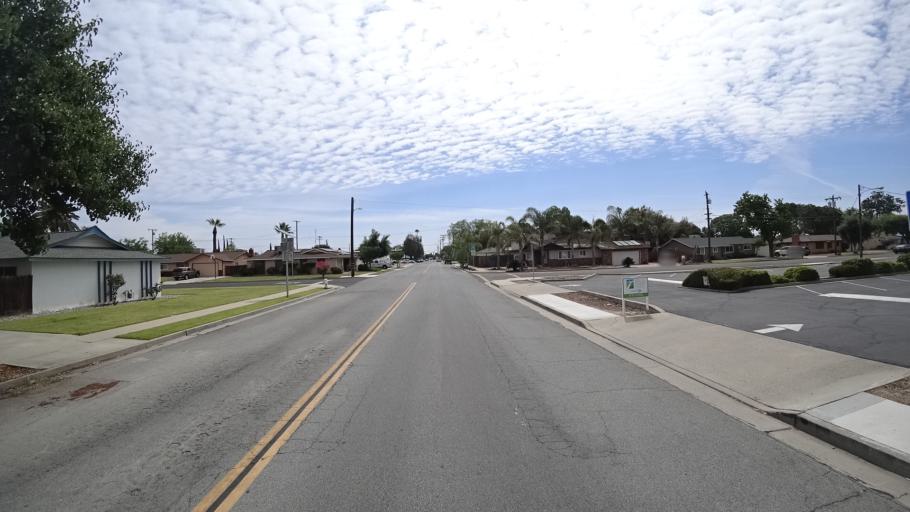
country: US
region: California
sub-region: Kings County
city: Hanford
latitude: 36.3518
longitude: -119.6476
